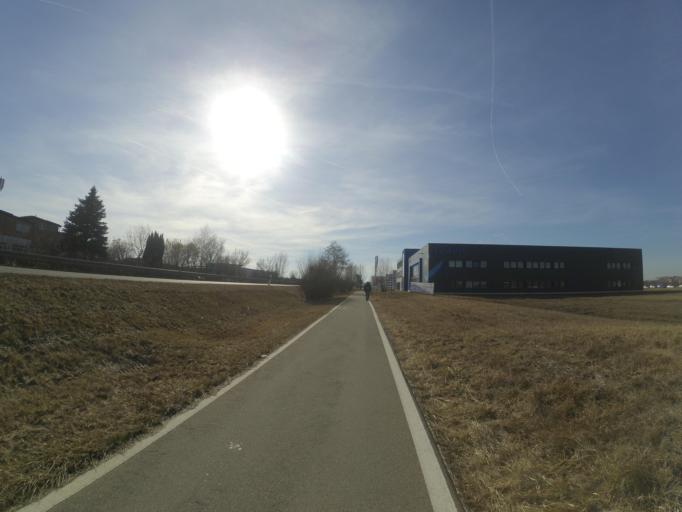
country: DE
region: Baden-Wuerttemberg
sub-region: Tuebingen Region
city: Friedrichshafen
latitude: 47.6640
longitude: 9.5044
